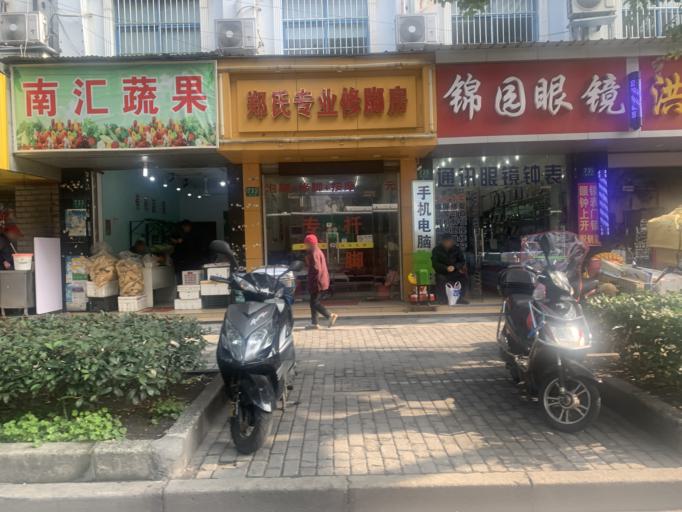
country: CN
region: Shanghai Shi
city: Huamu
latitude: 31.1873
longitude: 121.5139
